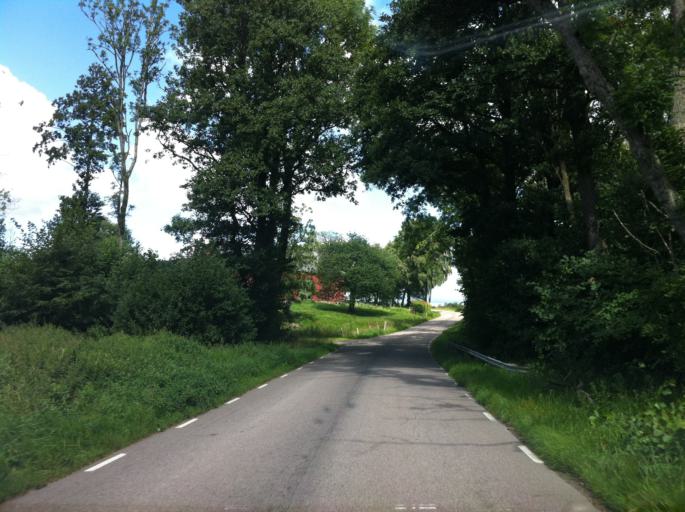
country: SE
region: Skane
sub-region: Svalovs Kommun
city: Kagerod
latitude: 56.0338
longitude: 13.1011
